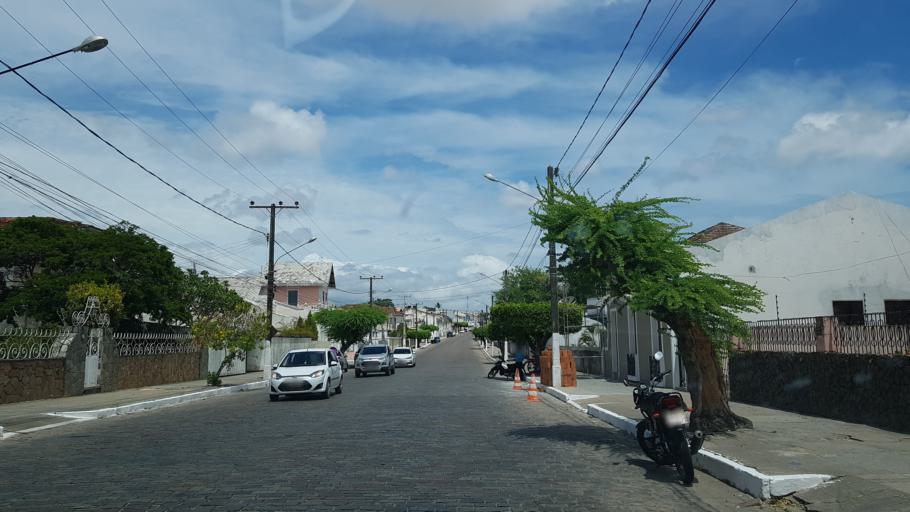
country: BR
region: Alagoas
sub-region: Penedo
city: Penedo
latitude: -10.2861
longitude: -36.5770
